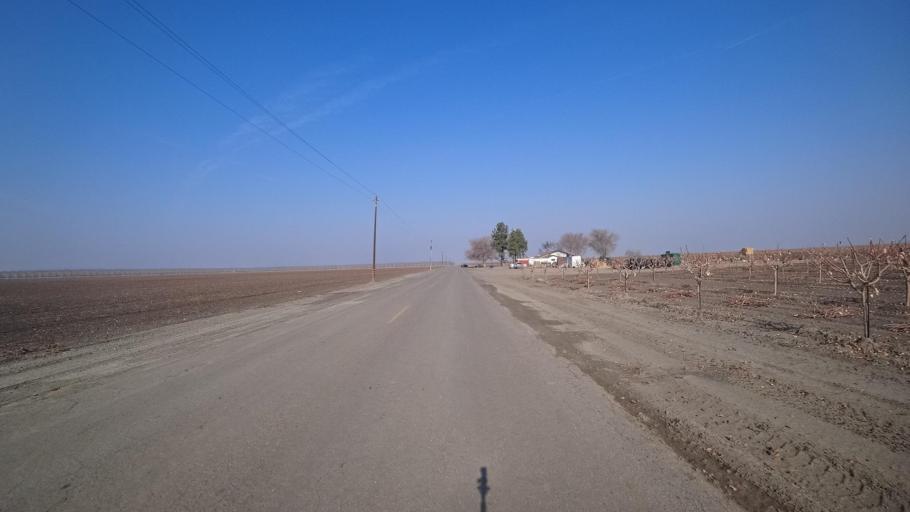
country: US
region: California
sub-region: Kern County
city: Buttonwillow
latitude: 35.3565
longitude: -119.4123
